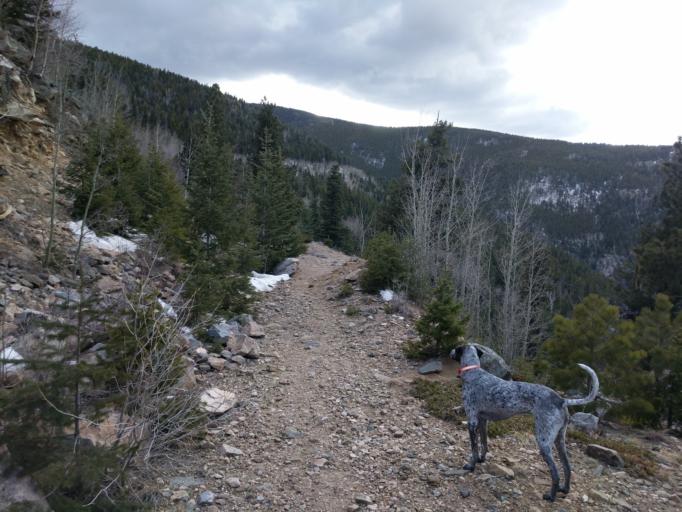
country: US
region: Colorado
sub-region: Clear Creek County
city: Idaho Springs
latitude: 39.7296
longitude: -105.4526
